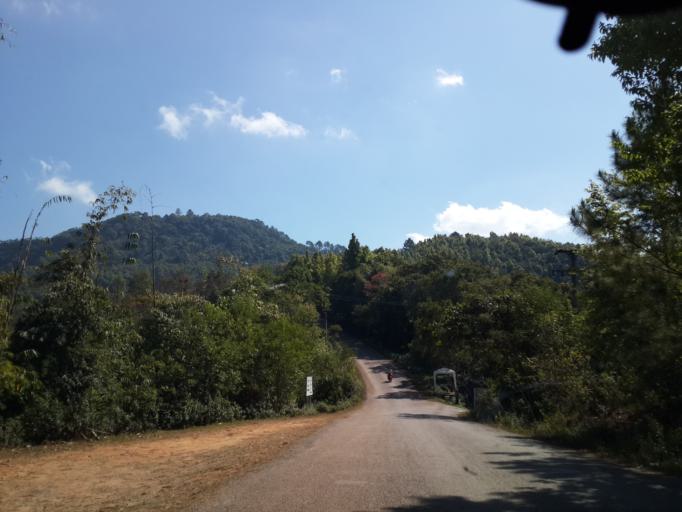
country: TH
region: Chiang Mai
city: Fang
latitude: 19.9197
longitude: 99.0483
